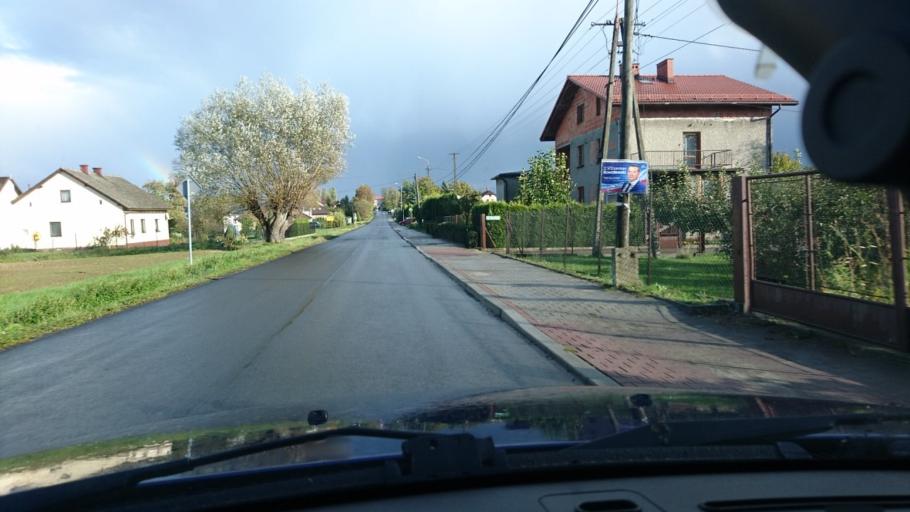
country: PL
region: Silesian Voivodeship
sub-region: Powiat bielski
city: Mazancowice
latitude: 49.8595
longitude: 19.0007
